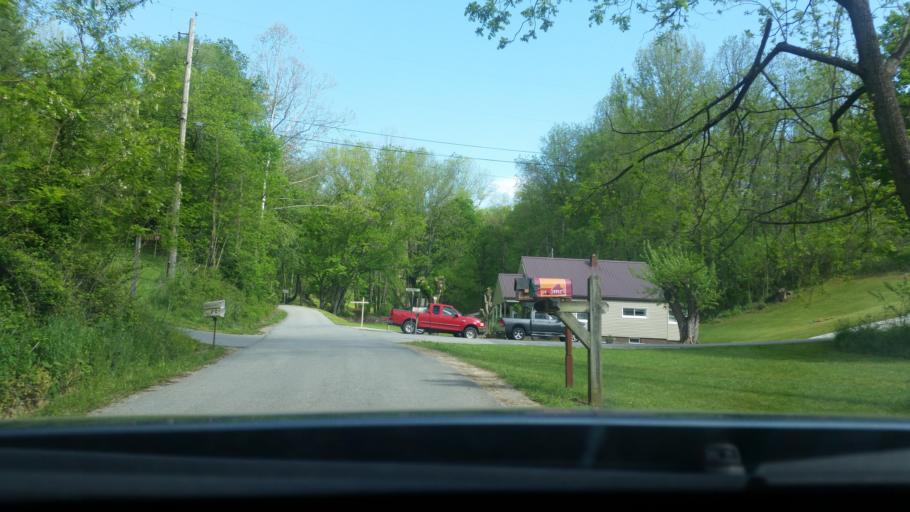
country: US
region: Virginia
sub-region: Giles County
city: Pembroke
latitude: 37.3176
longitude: -80.6289
